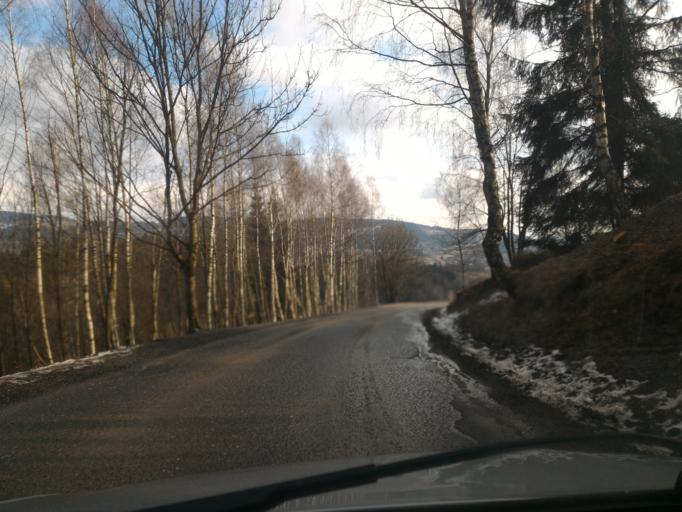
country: CZ
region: Liberecky
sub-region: Okres Jablonec nad Nisou
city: Desna
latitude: 50.7563
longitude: 15.2986
